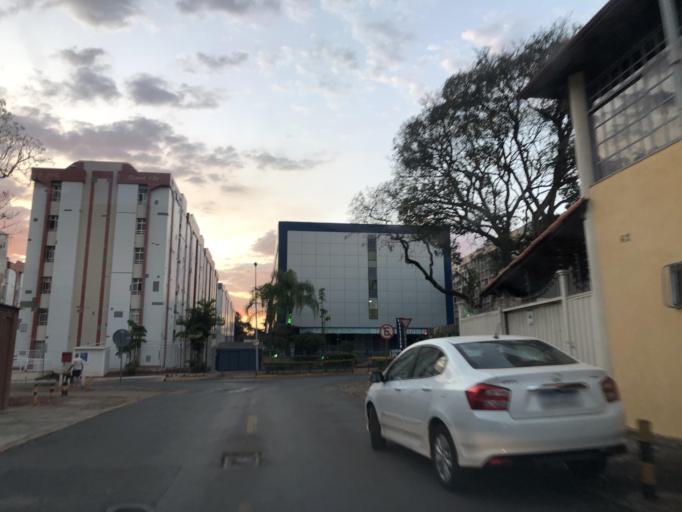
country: BR
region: Federal District
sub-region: Brasilia
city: Brasilia
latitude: -15.8169
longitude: -47.9163
